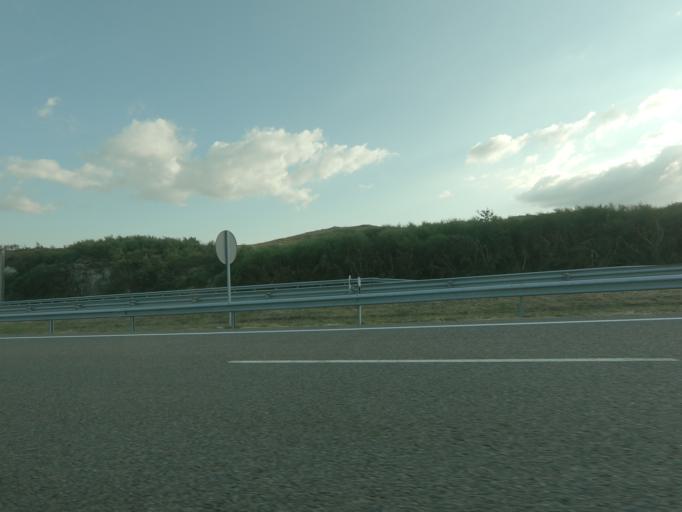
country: ES
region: Galicia
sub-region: Provincia de Ourense
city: Cualedro
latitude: 41.9861
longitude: -7.5492
